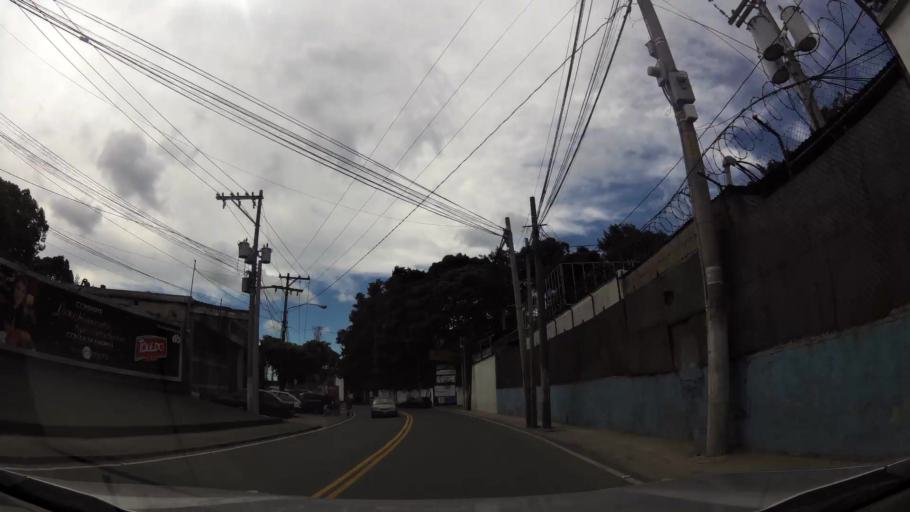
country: GT
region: Guatemala
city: Guatemala City
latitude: 14.6003
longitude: -90.5364
